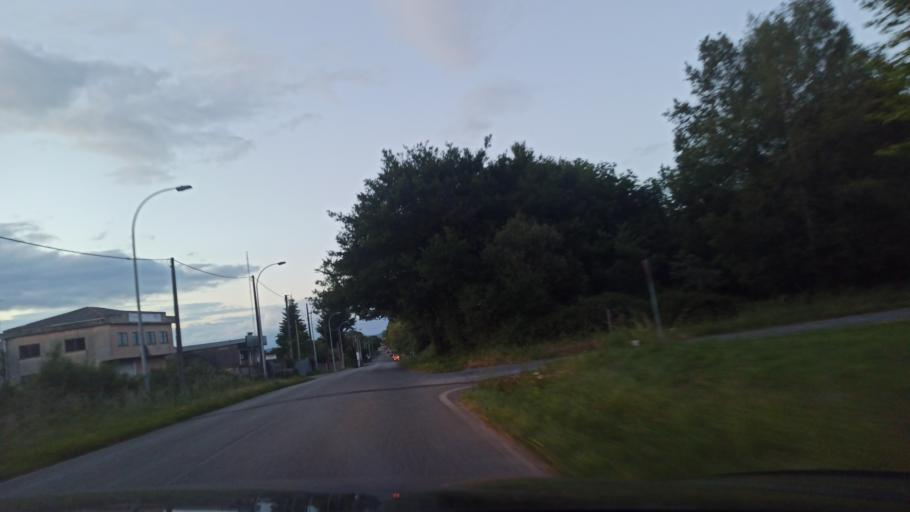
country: ES
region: Galicia
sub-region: Provincia de Lugo
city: Lugo
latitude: 42.9867
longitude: -7.5809
